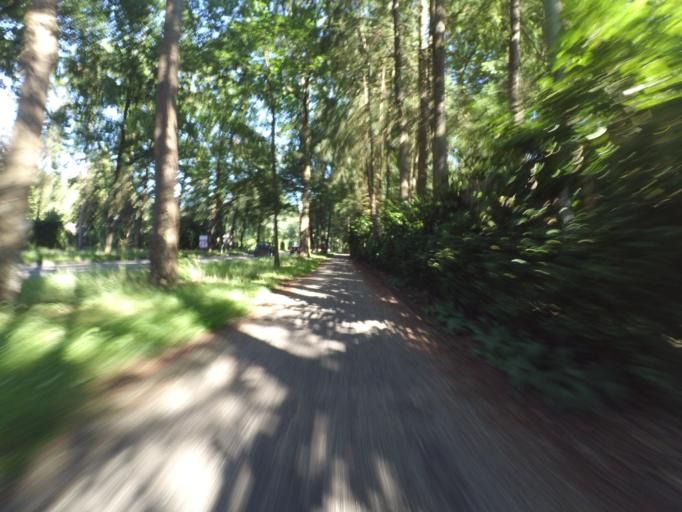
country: NL
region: Utrecht
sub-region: Gemeente Utrechtse Heuvelrug
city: Driebergen-Rijsenburg
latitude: 52.0546
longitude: 5.3031
